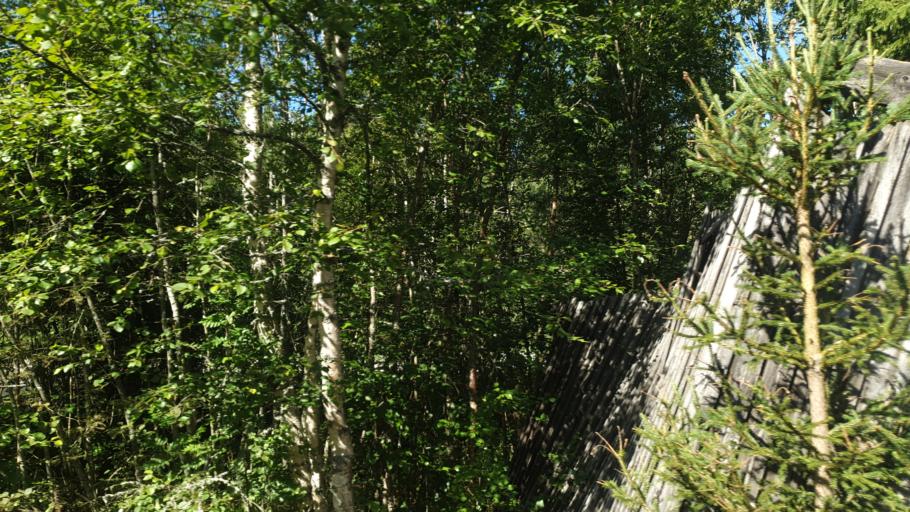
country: NO
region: Sor-Trondelag
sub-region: Orkdal
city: Orkanger
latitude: 63.1849
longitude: 9.7723
